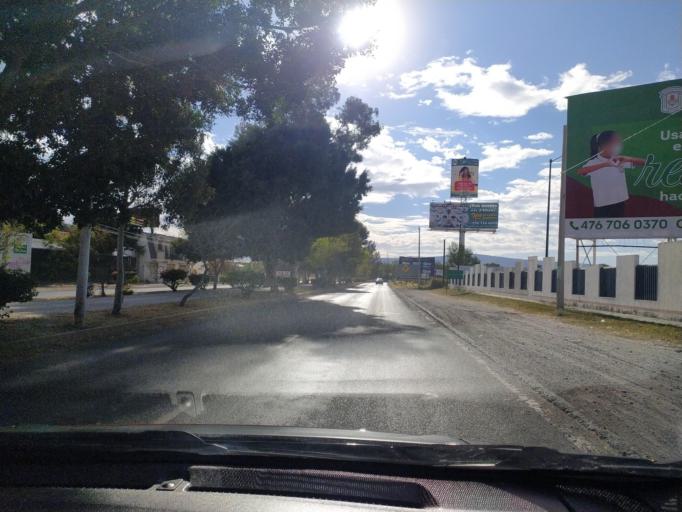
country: LA
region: Oudomxai
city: Muang La
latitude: 21.0323
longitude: 101.8299
